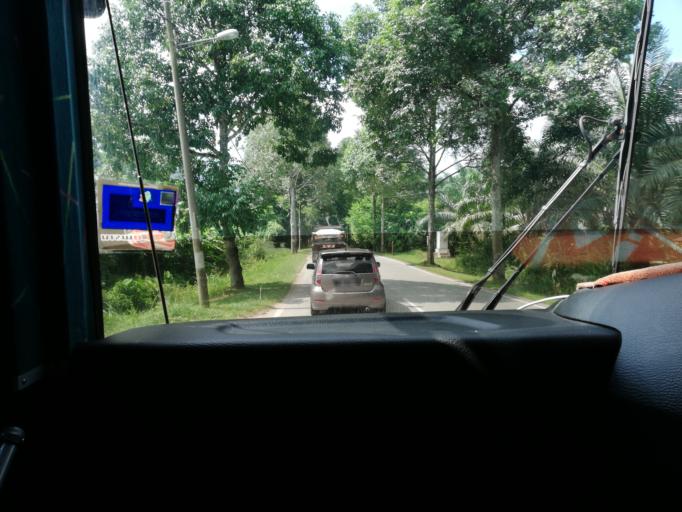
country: MY
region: Penang
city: Nibong Tebal
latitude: 5.2218
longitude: 100.6080
